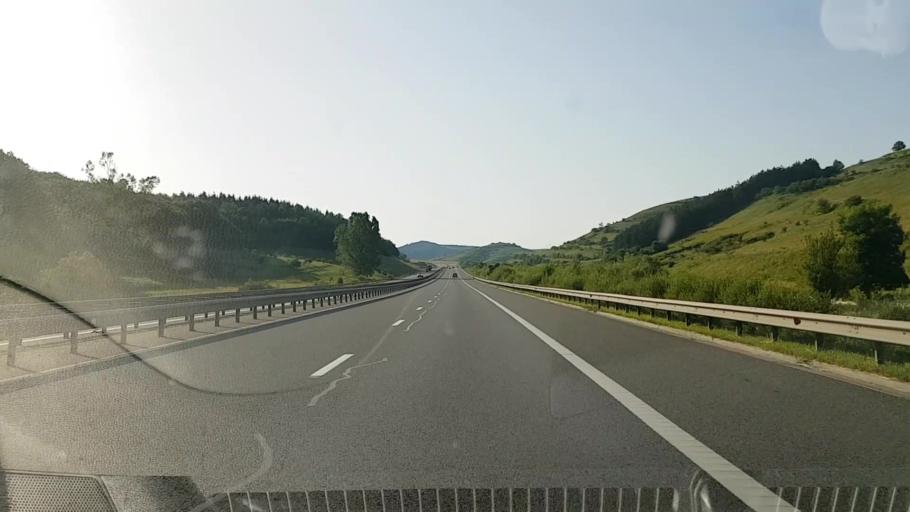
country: RO
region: Cluj
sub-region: Comuna Savadisla
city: Savadisla
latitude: 46.6749
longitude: 23.4805
